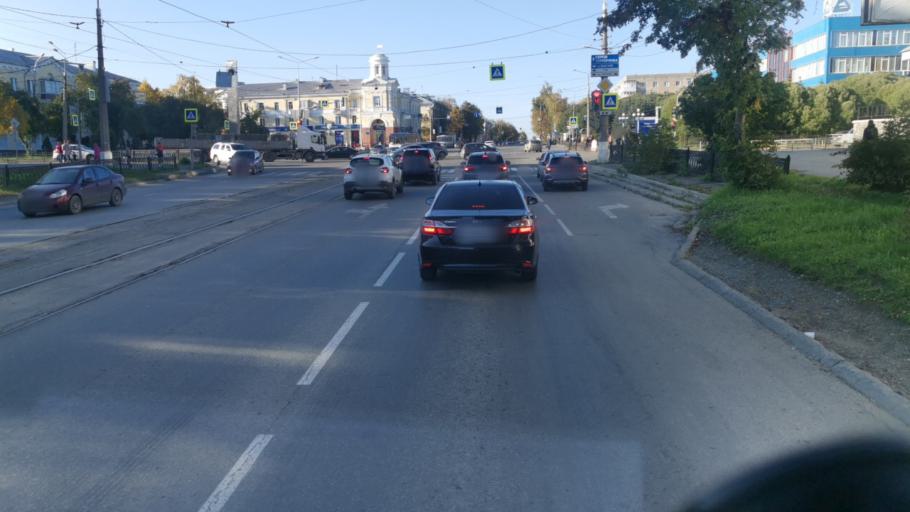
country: RU
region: Sverdlovsk
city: Nizhniy Tagil
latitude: 57.9174
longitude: 59.9448
